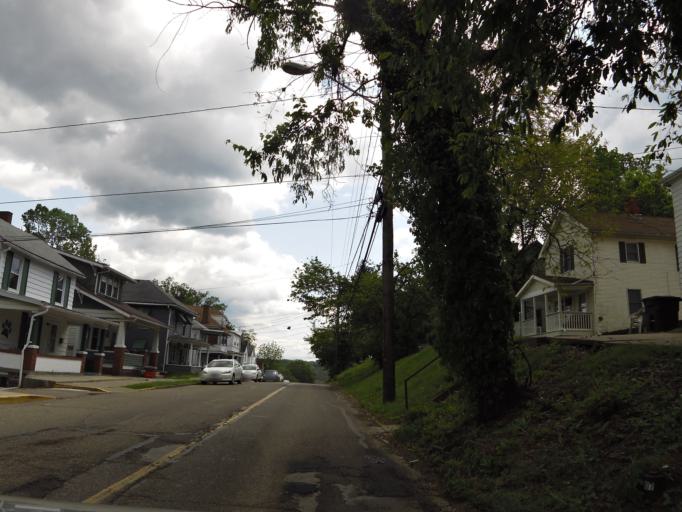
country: US
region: Ohio
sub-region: Athens County
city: Athens
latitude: 39.3320
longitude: -82.1061
